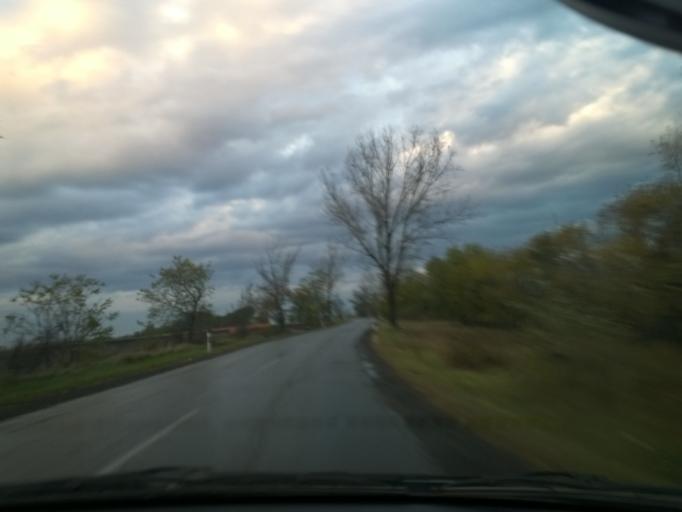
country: HU
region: Bacs-Kiskun
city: Szalkszentmarton
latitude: 46.9637
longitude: 18.9823
